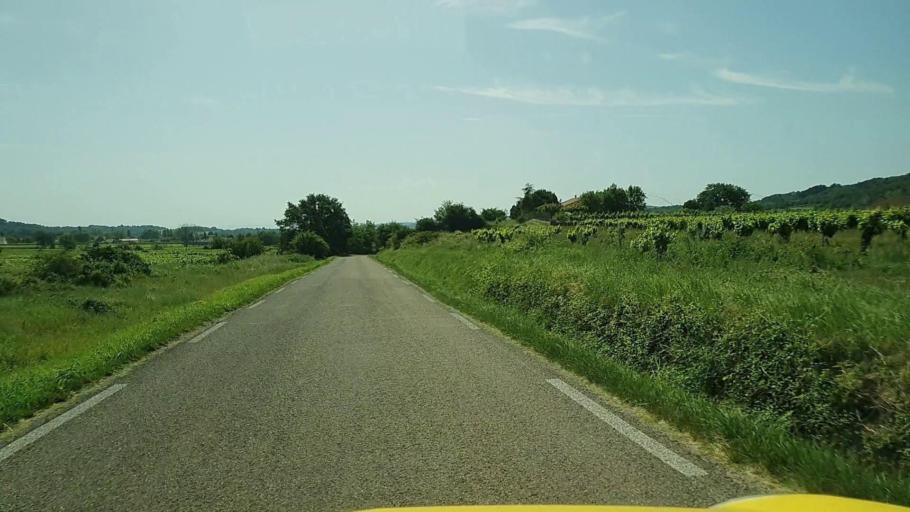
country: FR
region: Languedoc-Roussillon
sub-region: Departement du Gard
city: Sabran
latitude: 44.1191
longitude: 4.5066
